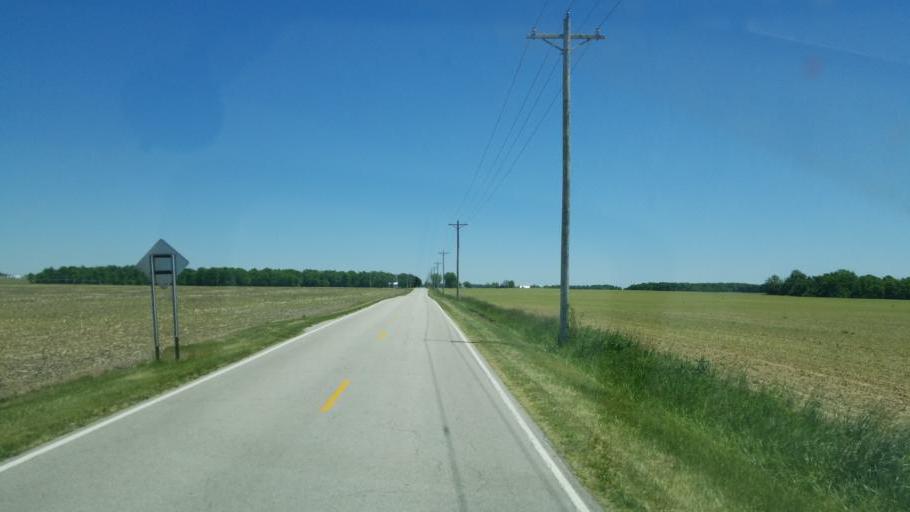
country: US
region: Ohio
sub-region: Darke County
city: Ansonia
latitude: 40.2649
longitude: -84.6985
